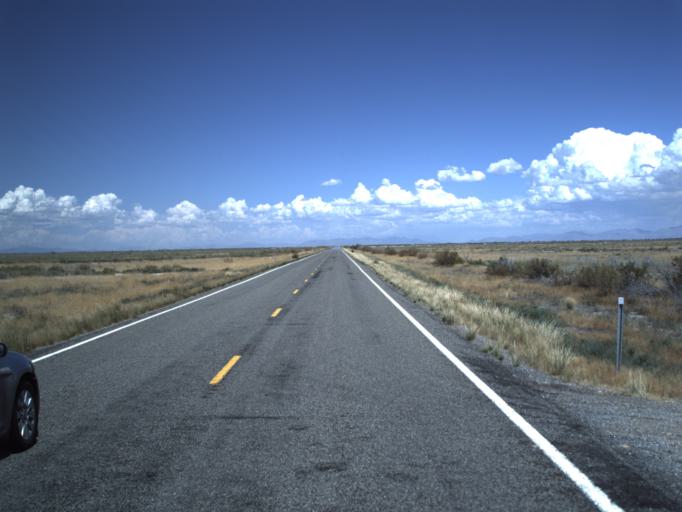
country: US
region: Utah
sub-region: Millard County
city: Delta
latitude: 39.2929
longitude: -112.8242
